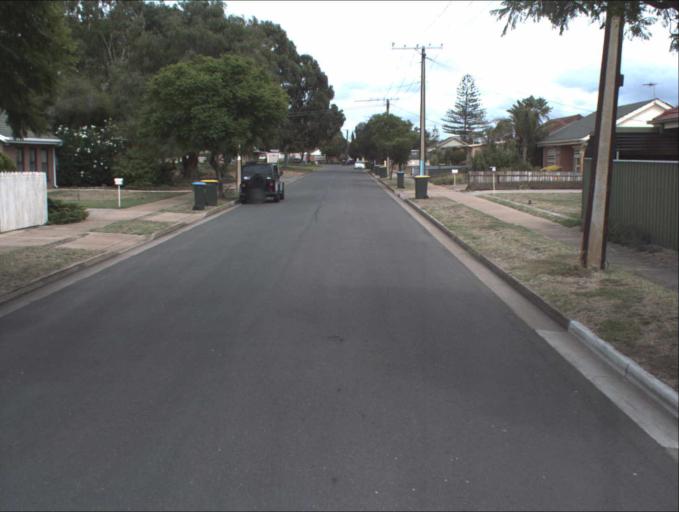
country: AU
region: South Australia
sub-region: Port Adelaide Enfield
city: Birkenhead
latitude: -34.8151
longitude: 138.5064
